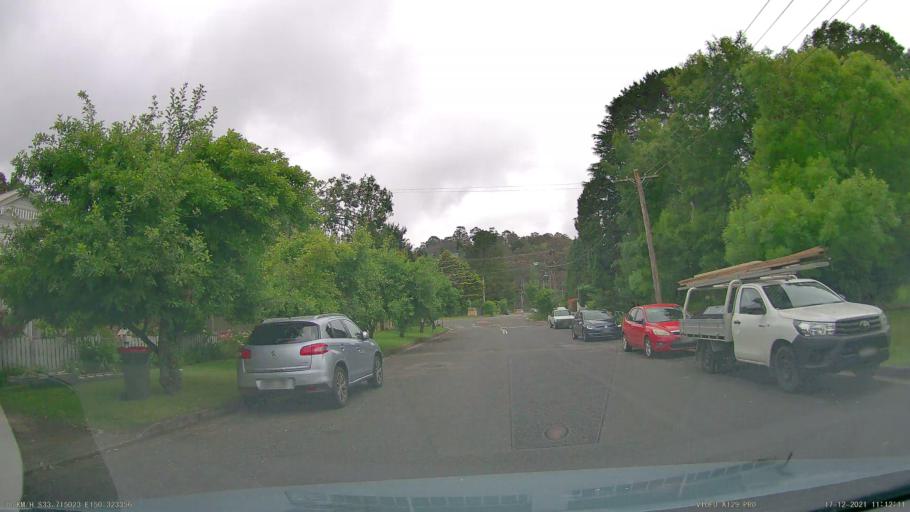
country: AU
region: New South Wales
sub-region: Blue Mountains Municipality
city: Leura
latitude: -33.7147
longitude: 150.3231
